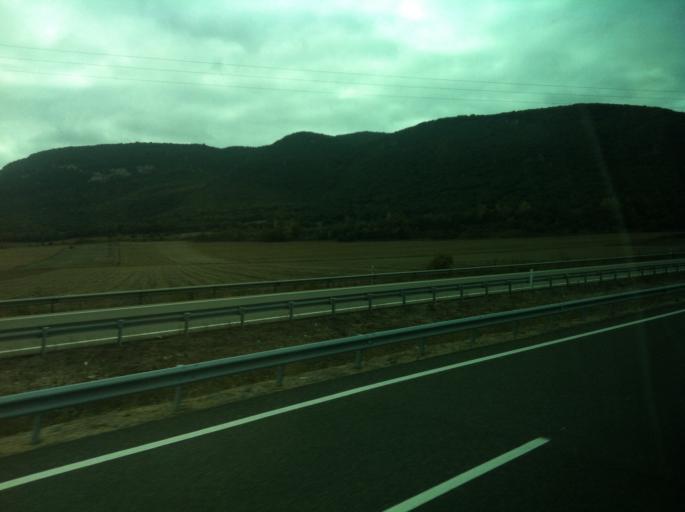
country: ES
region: Castille and Leon
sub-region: Provincia de Burgos
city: Ameyugo
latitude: 42.6565
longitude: -3.0507
